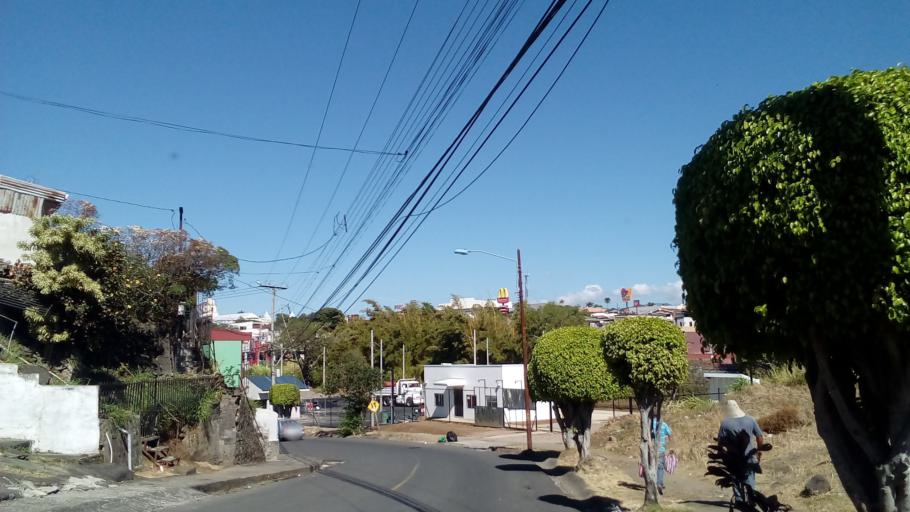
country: CR
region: Heredia
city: Heredia
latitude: 9.9945
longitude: -84.1109
